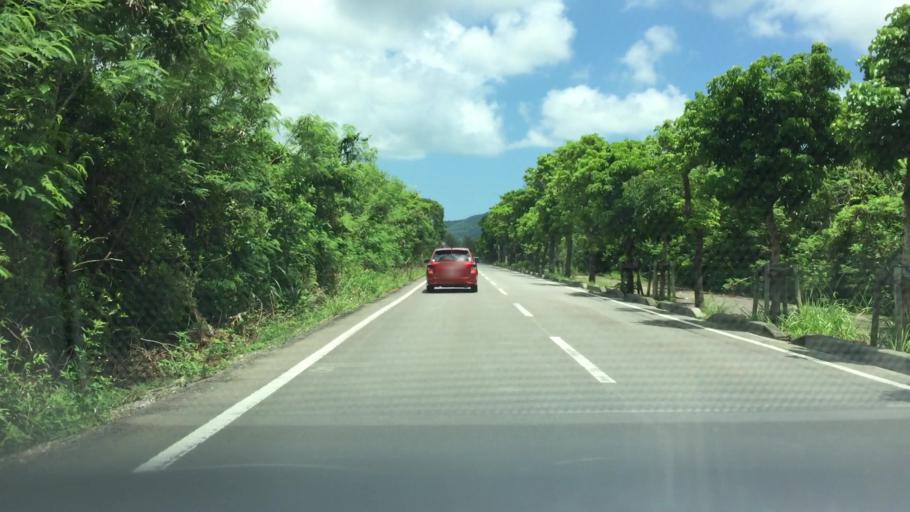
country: JP
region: Okinawa
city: Ishigaki
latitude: 24.3973
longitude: 124.1410
